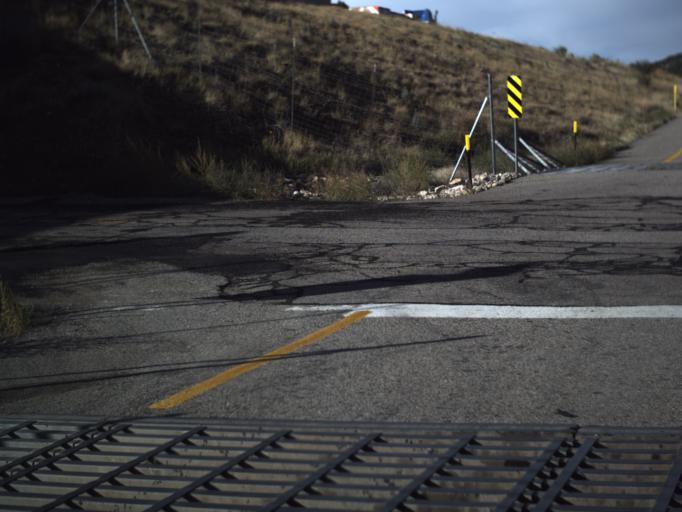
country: US
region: Utah
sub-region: Washington County
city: Toquerville
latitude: 37.4050
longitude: -113.2376
